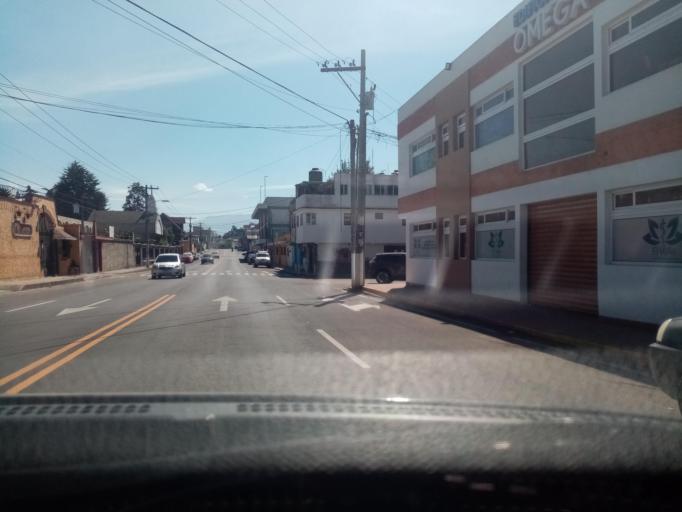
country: GT
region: Quetzaltenango
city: Quetzaltenango
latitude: 14.8464
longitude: -91.5163
